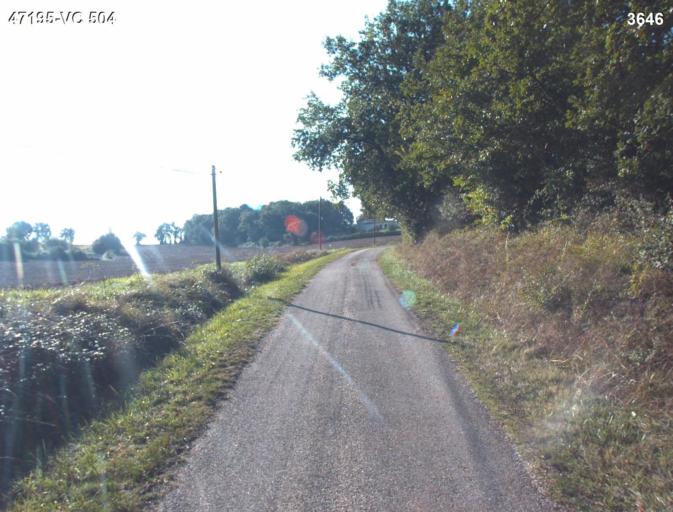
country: FR
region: Aquitaine
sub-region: Departement du Lot-et-Garonne
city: Vianne
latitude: 44.1769
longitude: 0.3438
